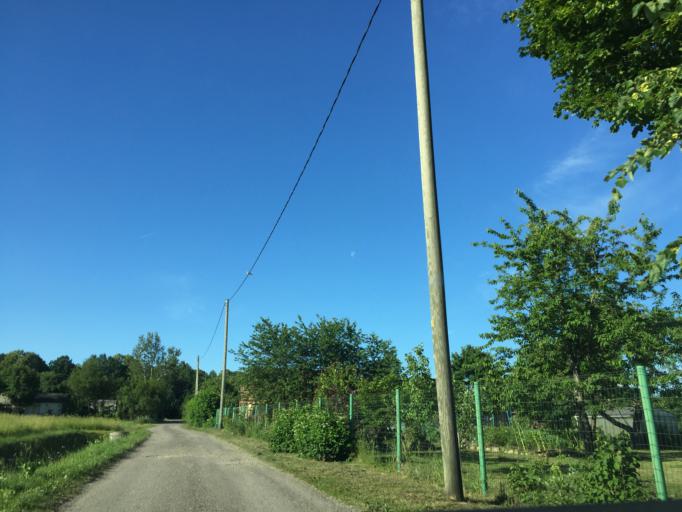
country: LV
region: Ventspils
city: Ventspils
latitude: 57.3651
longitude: 21.5998
